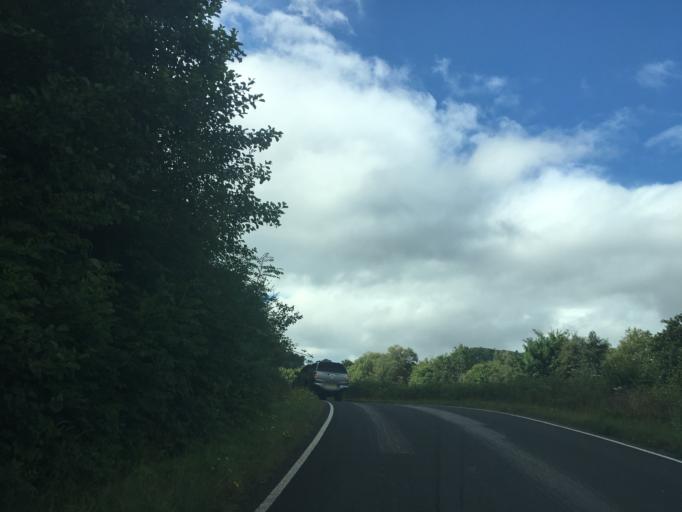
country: GB
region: Scotland
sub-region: Argyll and Bute
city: Ardrishaig
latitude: 56.0779
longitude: -5.5434
